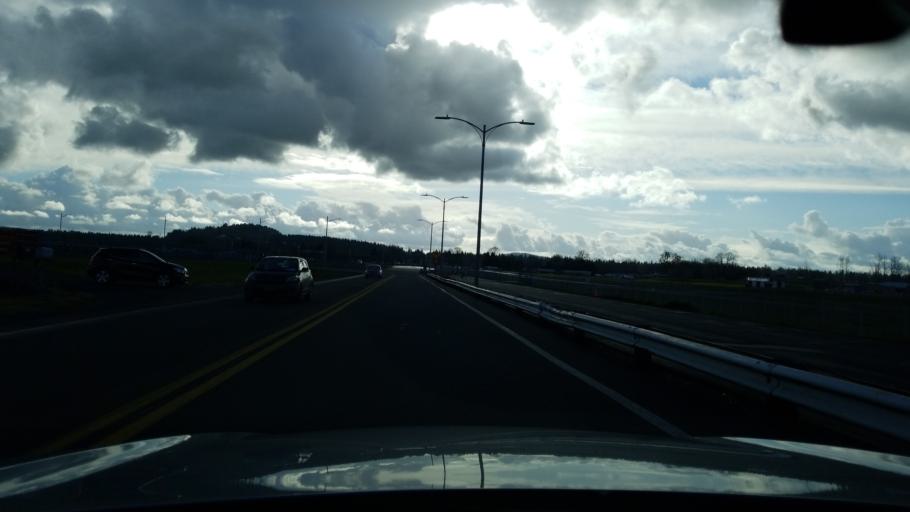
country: US
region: Washington
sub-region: Clark County
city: Orchards
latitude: 45.5819
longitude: -122.5777
